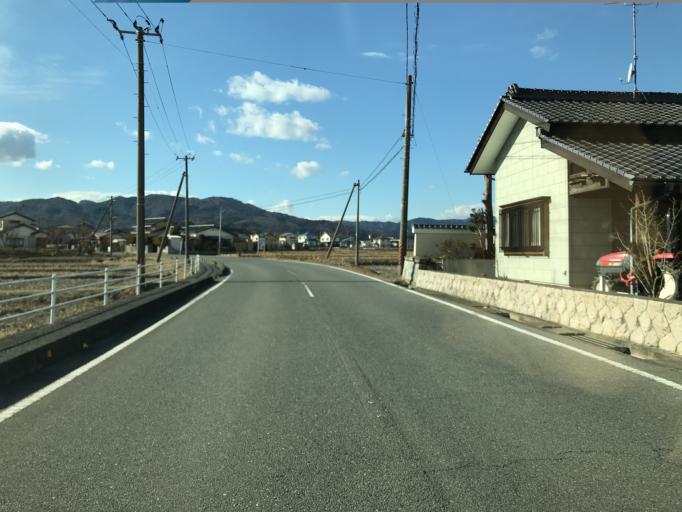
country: JP
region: Fukushima
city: Iwaki
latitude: 37.1243
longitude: 140.8662
